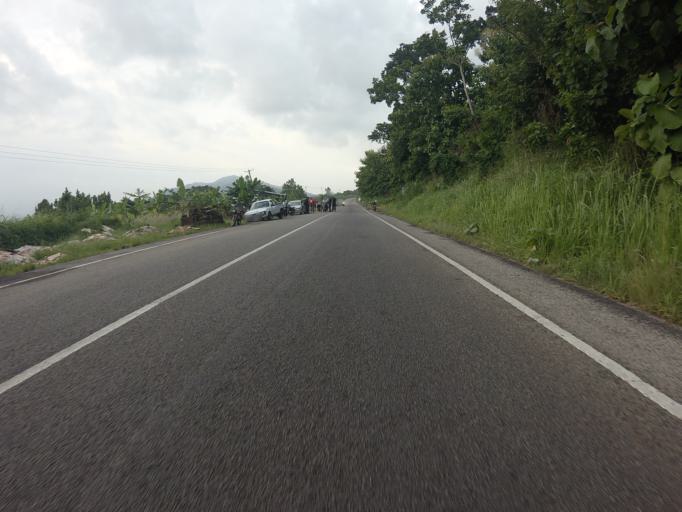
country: GH
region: Volta
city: Ho
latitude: 6.6219
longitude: 0.4580
